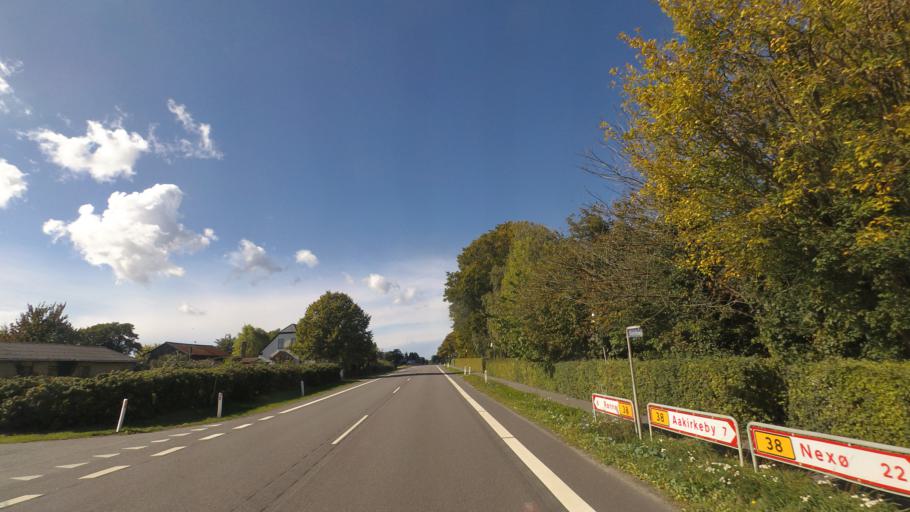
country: DK
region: Capital Region
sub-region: Bornholm Kommune
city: Ronne
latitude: 55.0711
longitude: 14.8110
